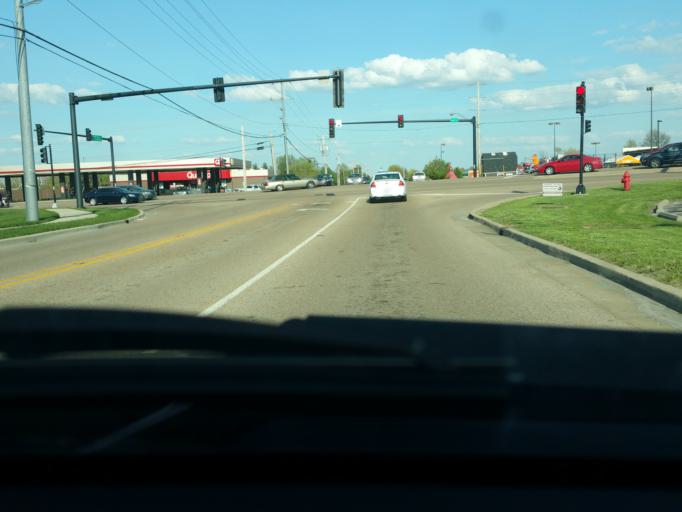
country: US
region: Illinois
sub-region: Madison County
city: Edwardsville
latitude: 38.7814
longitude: -89.9521
